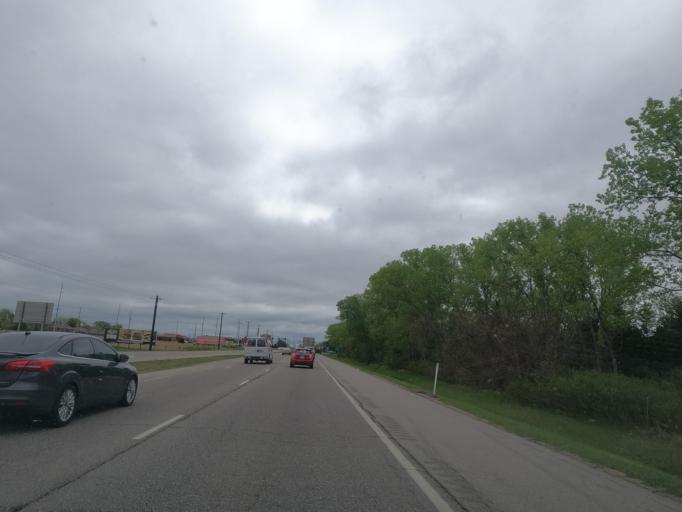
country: US
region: Kansas
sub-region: Butler County
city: Andover
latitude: 37.6793
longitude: -97.1745
